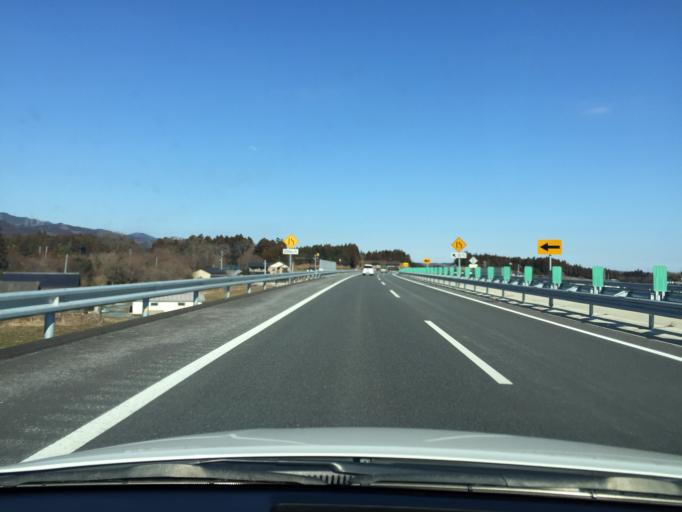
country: JP
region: Fukushima
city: Namie
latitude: 37.5317
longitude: 140.9411
